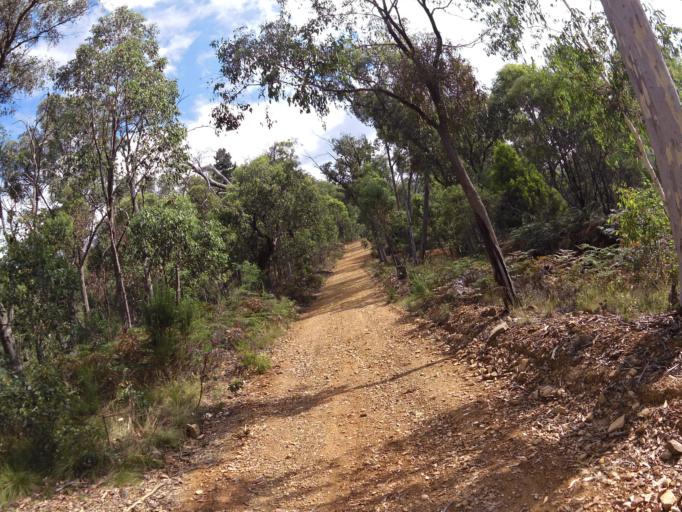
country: AU
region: Victoria
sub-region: Alpine
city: Mount Beauty
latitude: -36.7750
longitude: 147.0156
